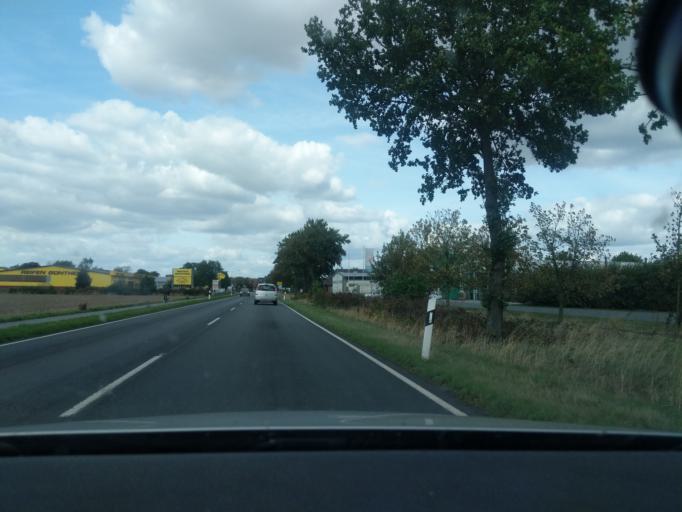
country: DE
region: Lower Saxony
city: Hoya
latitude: 52.7951
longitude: 9.1354
